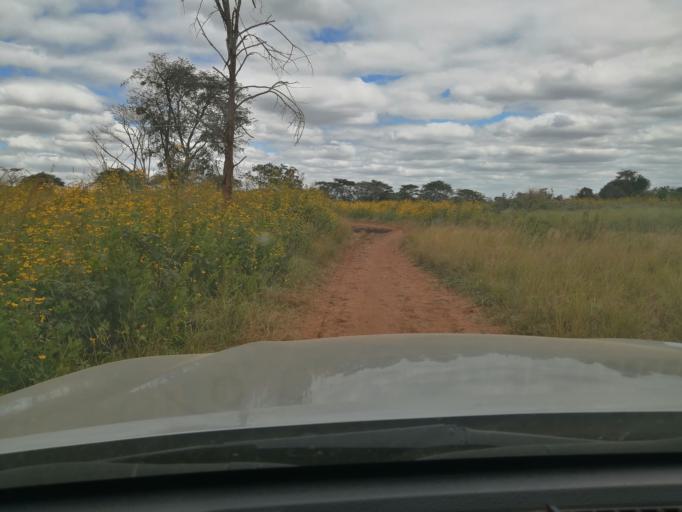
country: ZM
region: Central
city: Mumbwa
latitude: -14.6119
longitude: 27.1910
